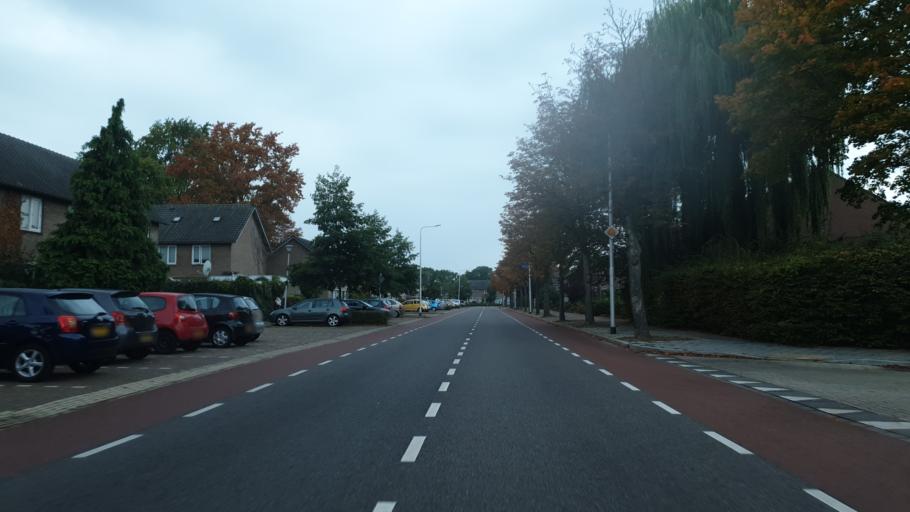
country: NL
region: Gelderland
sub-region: Gemeente Nijmegen
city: Lindenholt
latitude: 51.8068
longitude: 5.8107
